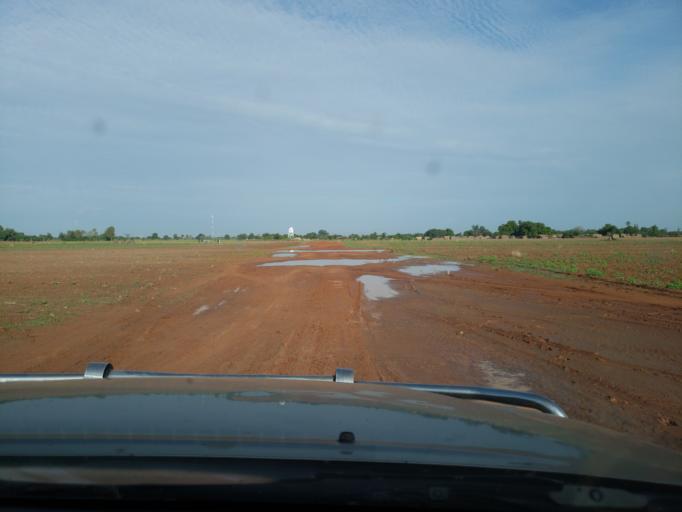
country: ML
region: Sikasso
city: Koutiala
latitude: 12.4234
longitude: -5.6712
